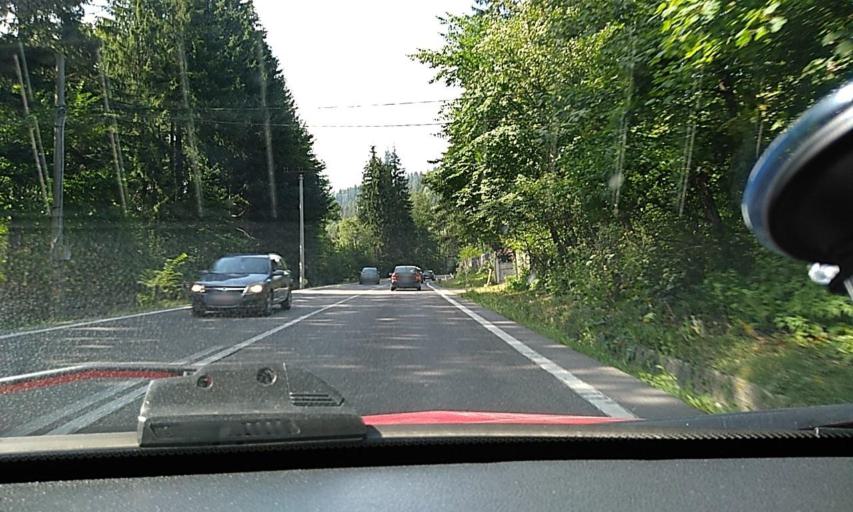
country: RO
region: Brasov
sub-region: Oras Predeal
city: Predeal
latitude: 45.5520
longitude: 25.5950
